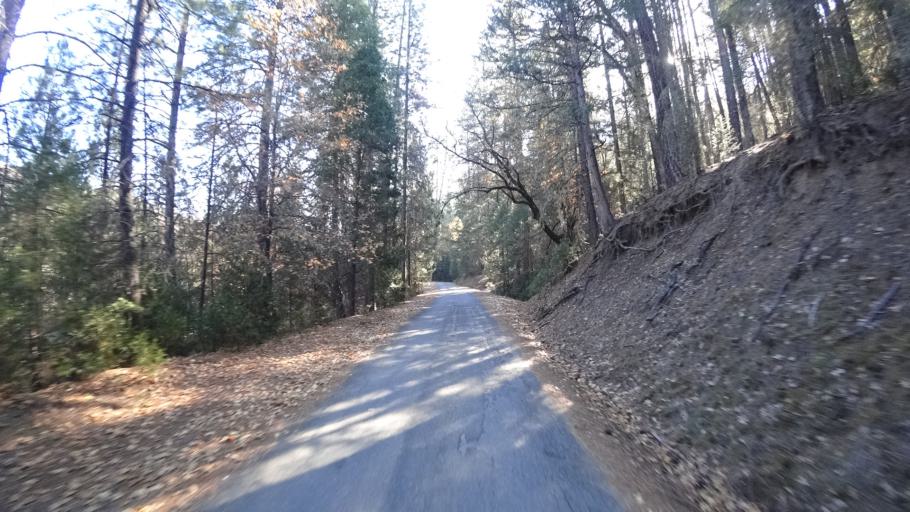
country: US
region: California
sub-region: Siskiyou County
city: Yreka
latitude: 41.8406
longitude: -122.8786
